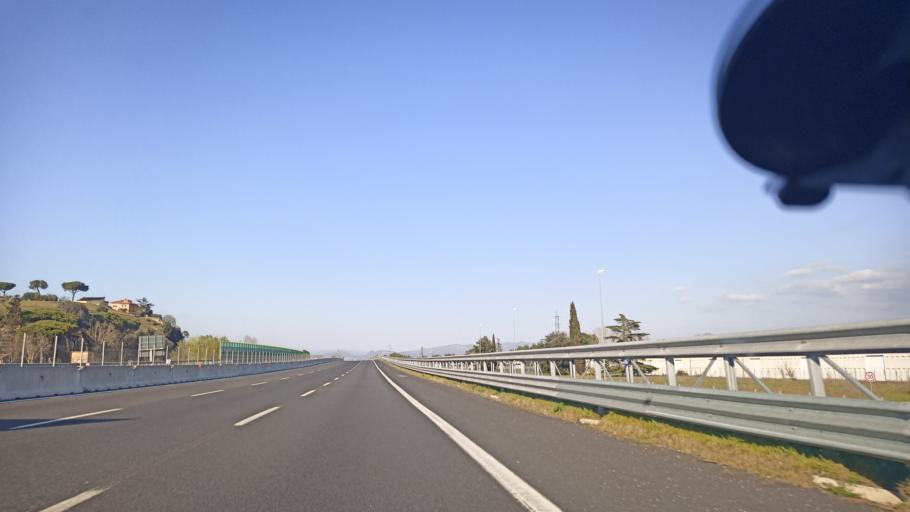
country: IT
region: Latium
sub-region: Citta metropolitana di Roma Capitale
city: Girardi-Bellavista-Terrazze
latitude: 42.0970
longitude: 12.5780
